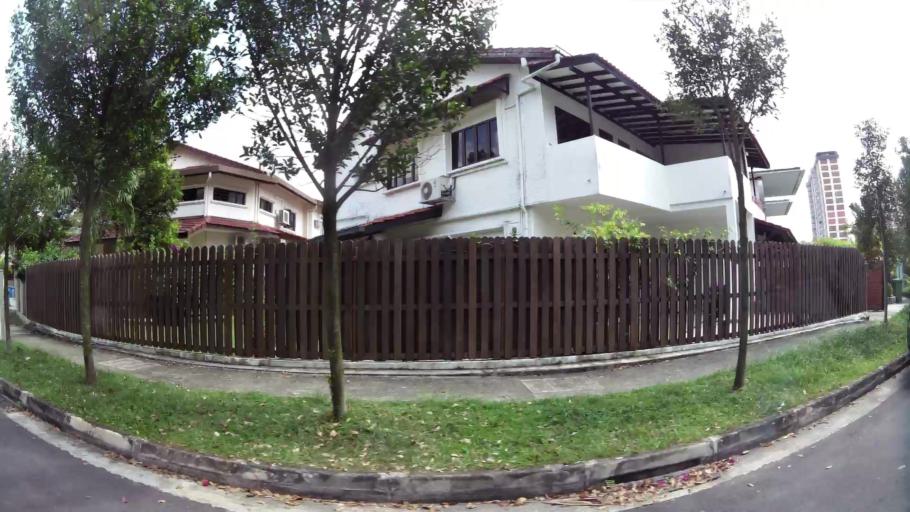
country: SG
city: Singapore
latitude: 1.3502
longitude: 103.8324
